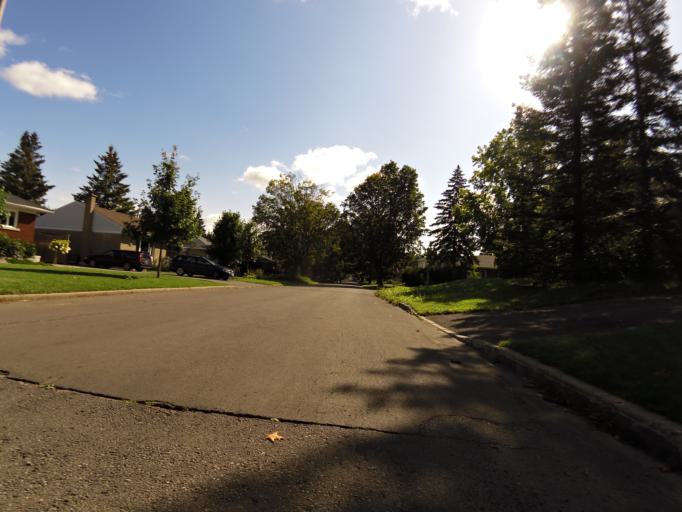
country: CA
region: Ontario
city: Ottawa
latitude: 45.3963
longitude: -75.6300
